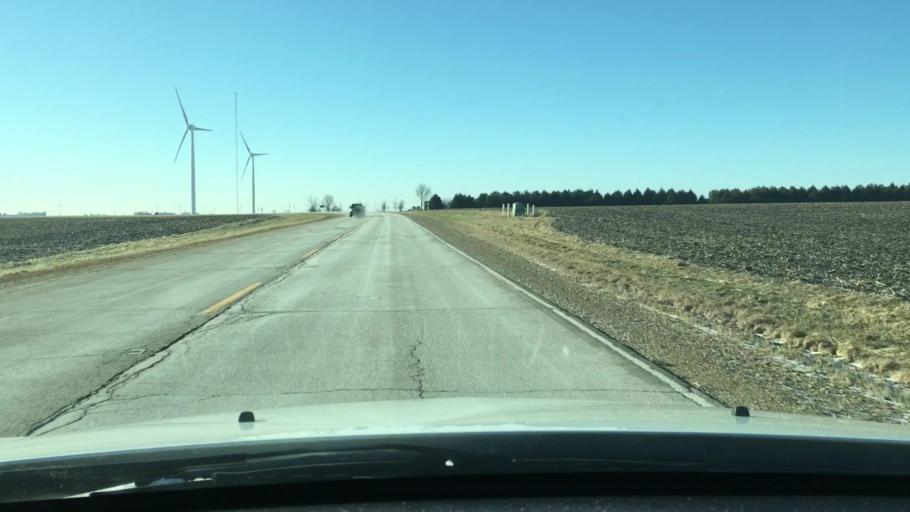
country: US
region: Illinois
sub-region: LaSalle County
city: Mendota
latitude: 41.6858
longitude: -89.1214
